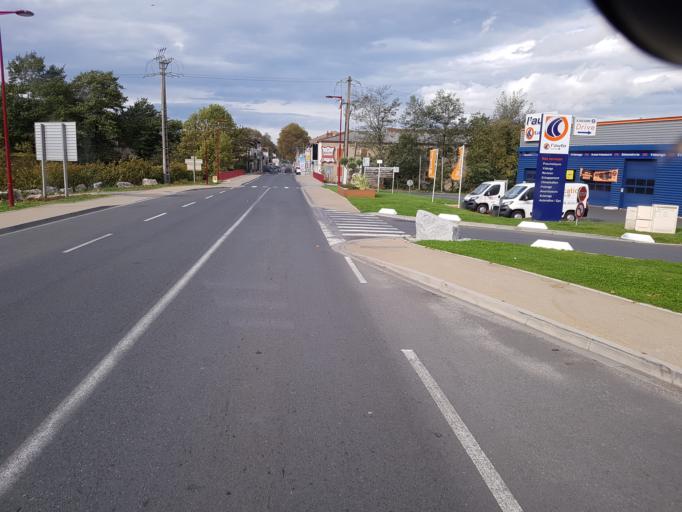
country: FR
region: Midi-Pyrenees
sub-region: Departement du Tarn
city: Pont-de-Larn
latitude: 43.4973
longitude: 2.3984
